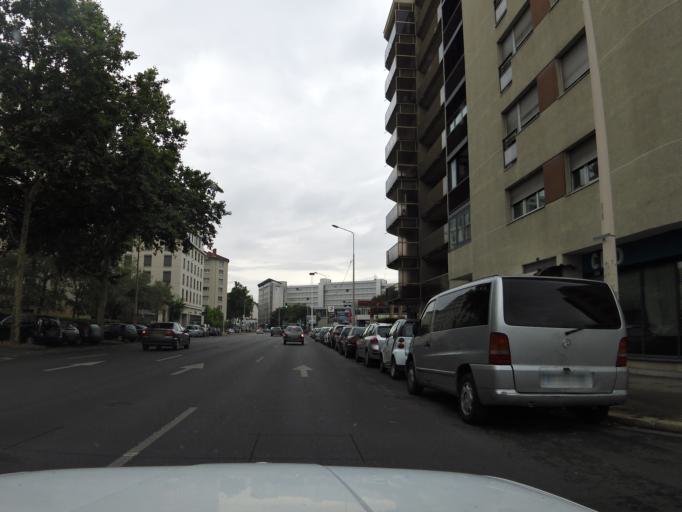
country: FR
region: Rhone-Alpes
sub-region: Departement du Rhone
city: Lyon
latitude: 45.7475
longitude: 4.8514
